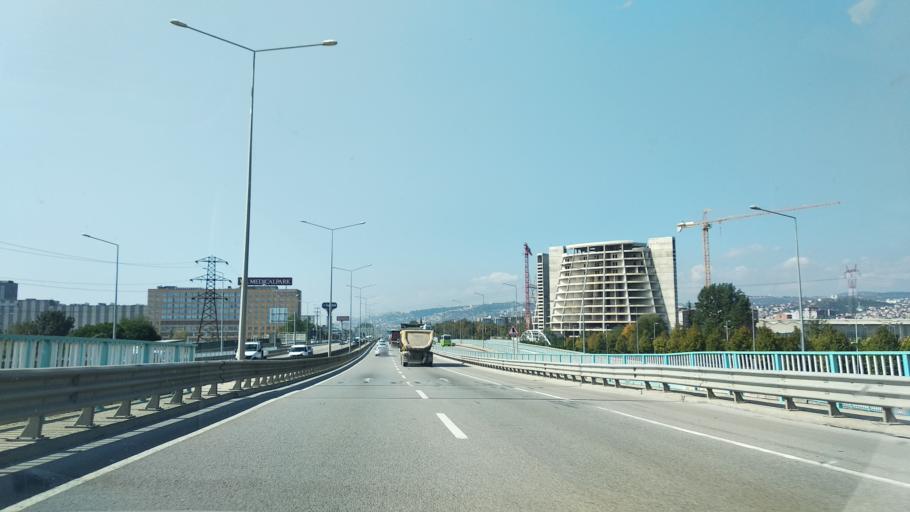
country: TR
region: Kocaeli
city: Kosekoy
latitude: 40.7587
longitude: 29.9867
